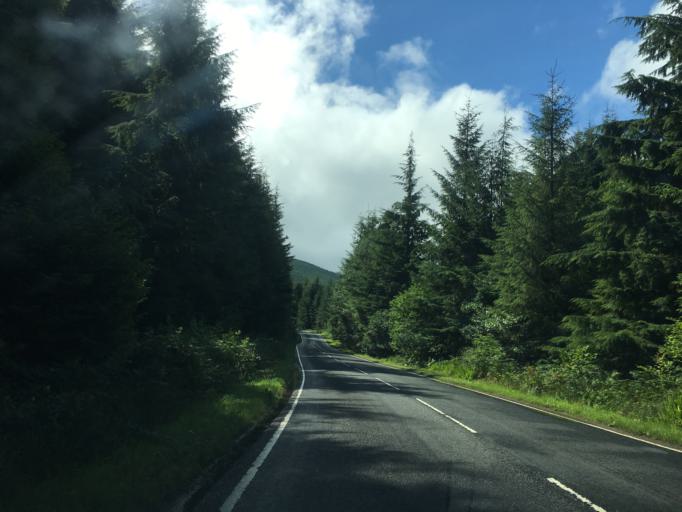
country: GB
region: Scotland
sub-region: Argyll and Bute
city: Dunoon
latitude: 55.9930
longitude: -4.9879
